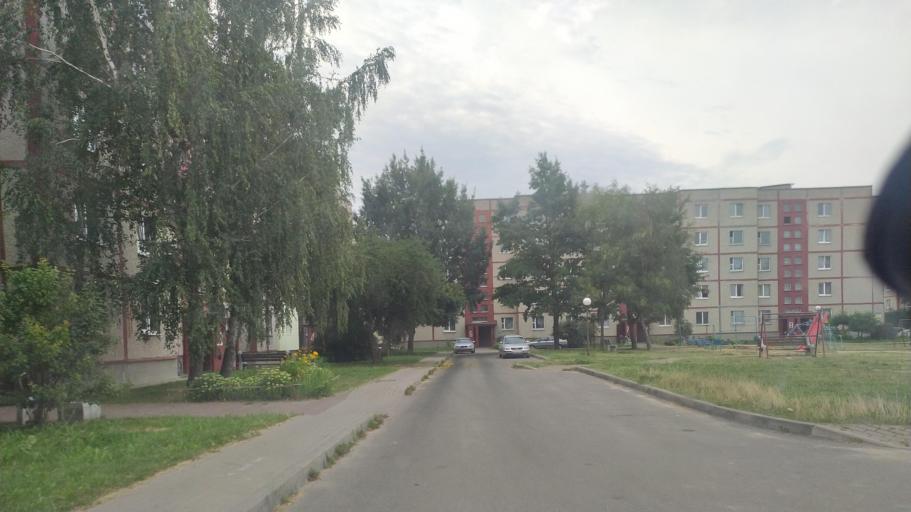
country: BY
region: Brest
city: Byaroza
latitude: 52.5395
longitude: 24.9737
